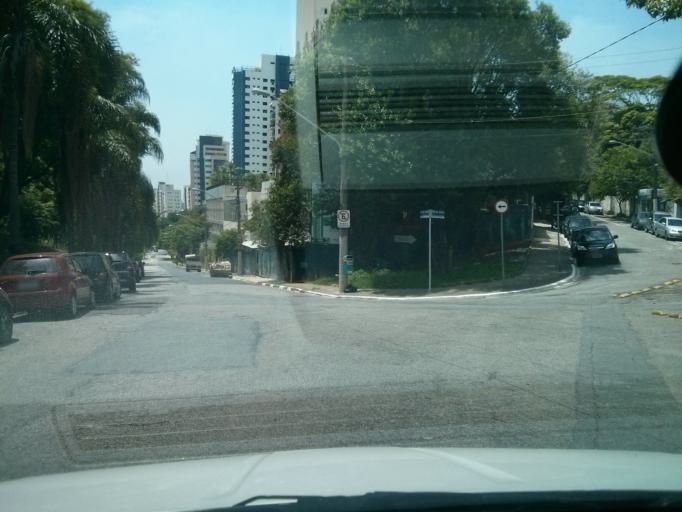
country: BR
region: Sao Paulo
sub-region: Sao Paulo
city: Sao Paulo
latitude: -23.5910
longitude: -46.6298
